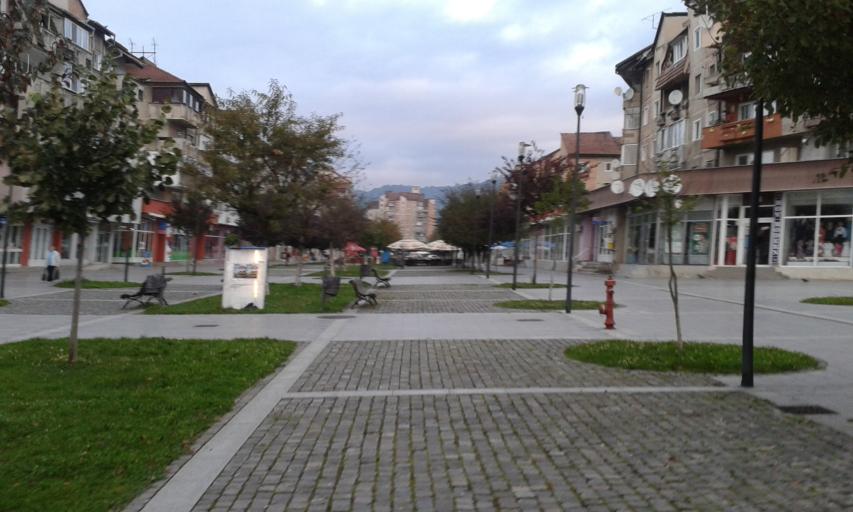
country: RO
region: Hunedoara
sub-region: Municipiul Petrosani
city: Petrosani
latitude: 45.4202
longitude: 23.3708
